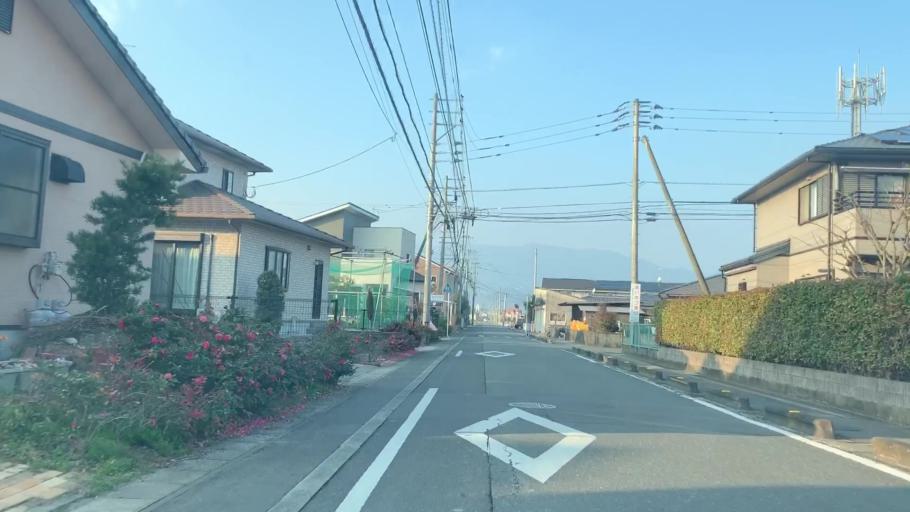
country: JP
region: Saga Prefecture
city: Saga-shi
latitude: 33.2718
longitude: 130.2289
